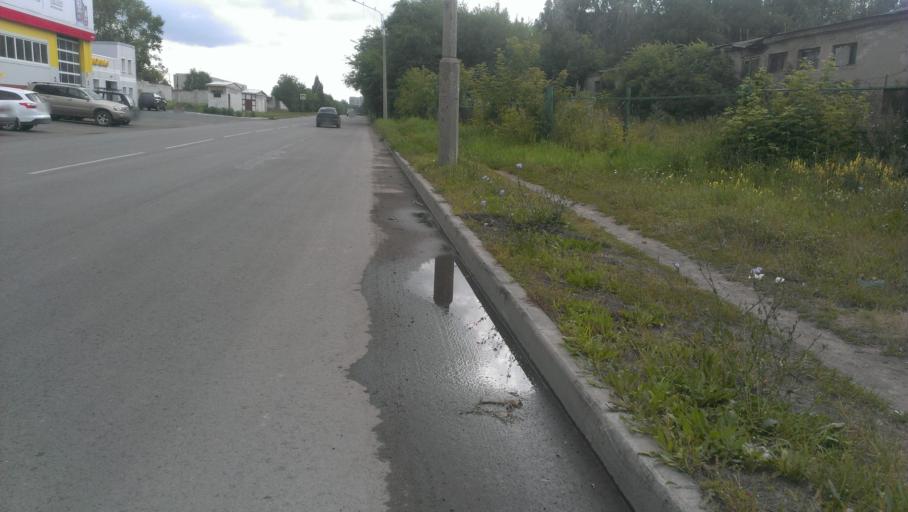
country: RU
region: Altai Krai
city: Yuzhnyy
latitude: 53.2549
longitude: 83.7020
